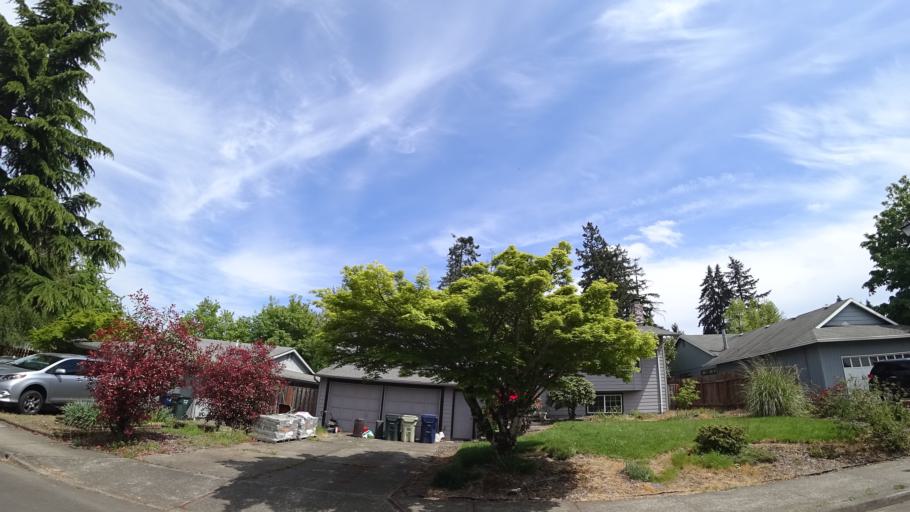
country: US
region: Oregon
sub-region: Washington County
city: Aloha
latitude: 45.4731
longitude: -122.8857
